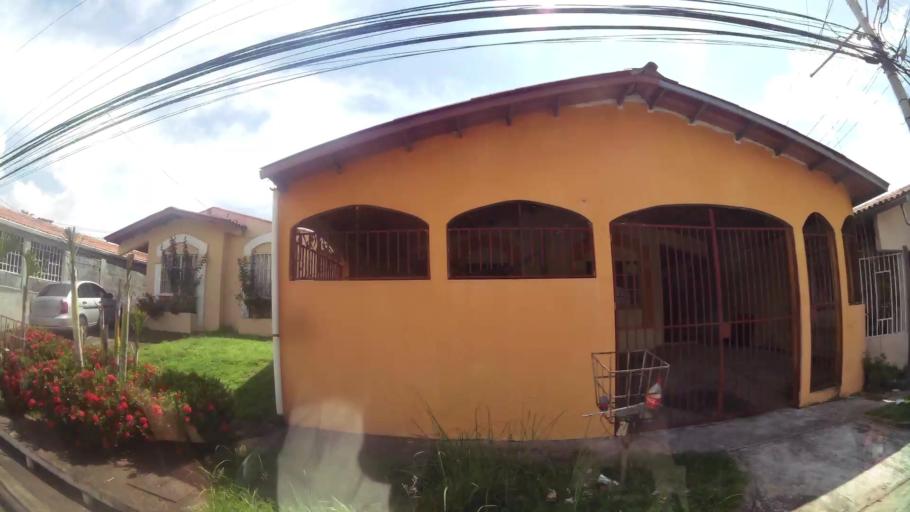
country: PA
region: Panama
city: San Vicente de Bique
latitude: 8.9176
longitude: -79.6911
